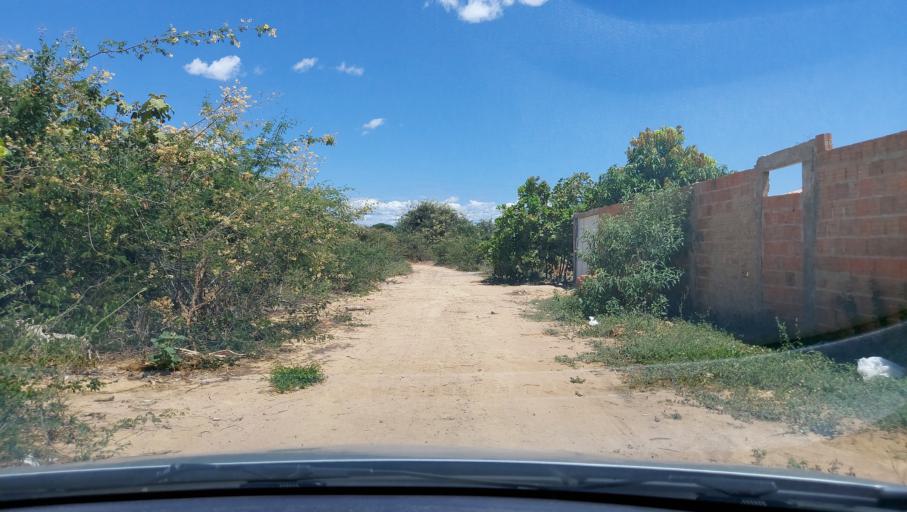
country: BR
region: Bahia
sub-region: Oliveira Dos Brejinhos
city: Beira Rio
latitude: -12.0069
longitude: -42.6357
